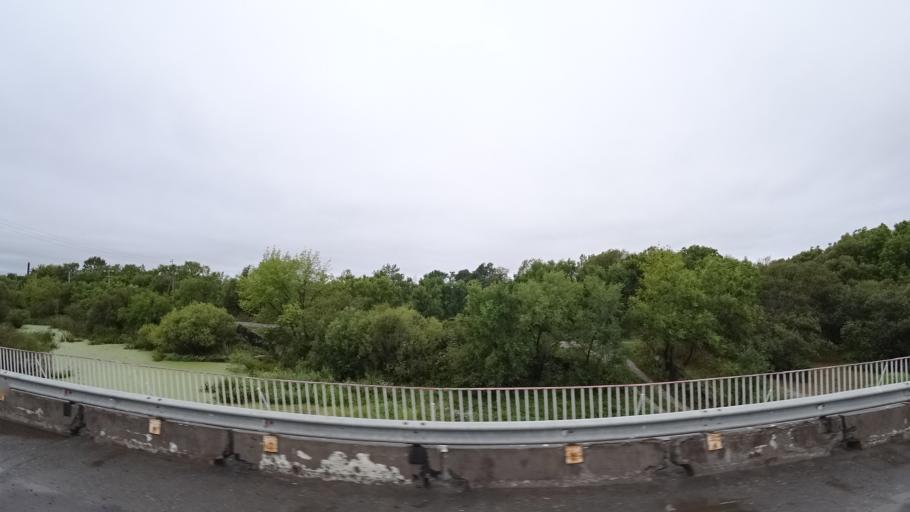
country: RU
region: Primorskiy
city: Monastyrishche
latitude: 44.2169
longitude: 132.4507
